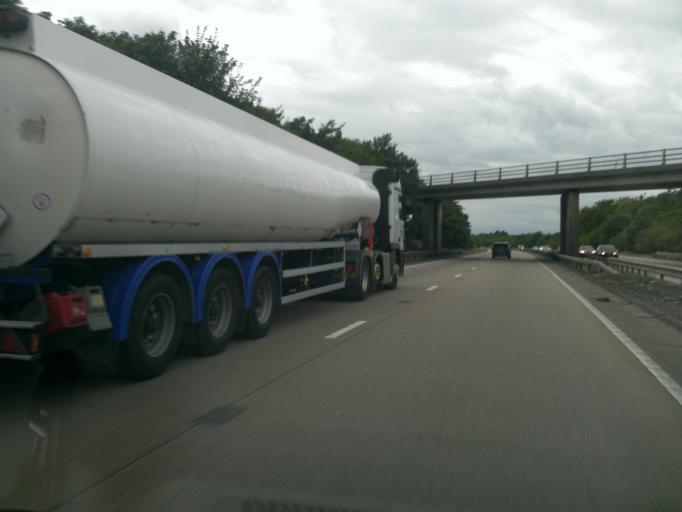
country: GB
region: England
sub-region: Essex
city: Alresford
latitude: 51.8907
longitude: 1.0124
